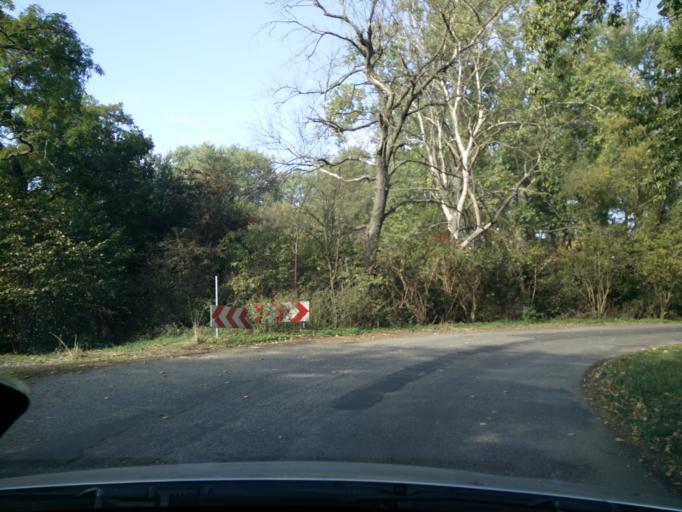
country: PL
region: Greater Poland Voivodeship
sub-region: Powiat sredzki
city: Dominowo
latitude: 52.2857
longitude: 17.3160
